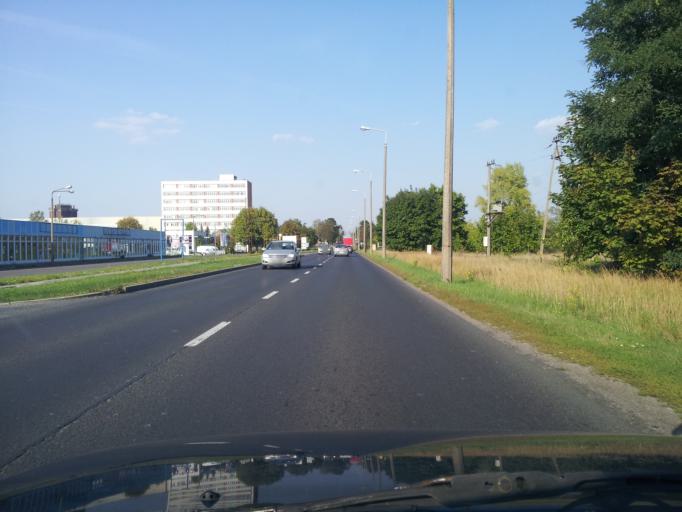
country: PL
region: Kujawsko-Pomorskie
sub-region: Torun
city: Torun
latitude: 52.9841
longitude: 18.5768
